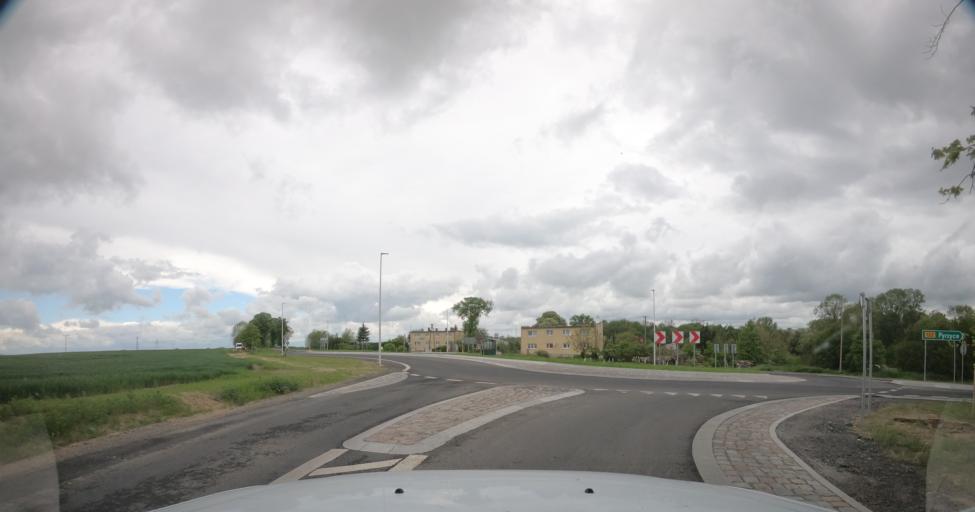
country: PL
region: West Pomeranian Voivodeship
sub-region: Powiat pyrzycki
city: Kozielice
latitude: 53.1233
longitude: 14.7961
